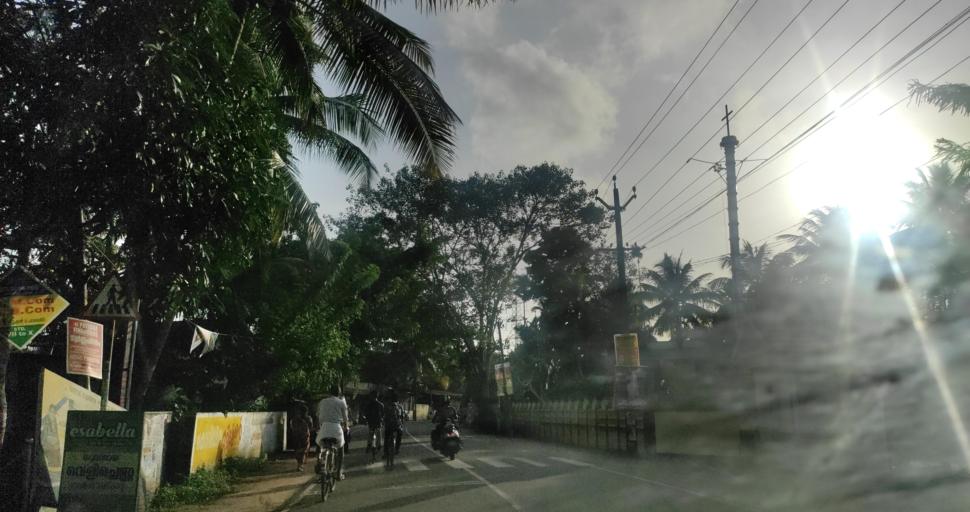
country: IN
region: Kerala
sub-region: Alappuzha
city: Shertallai
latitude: 9.6084
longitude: 76.3368
